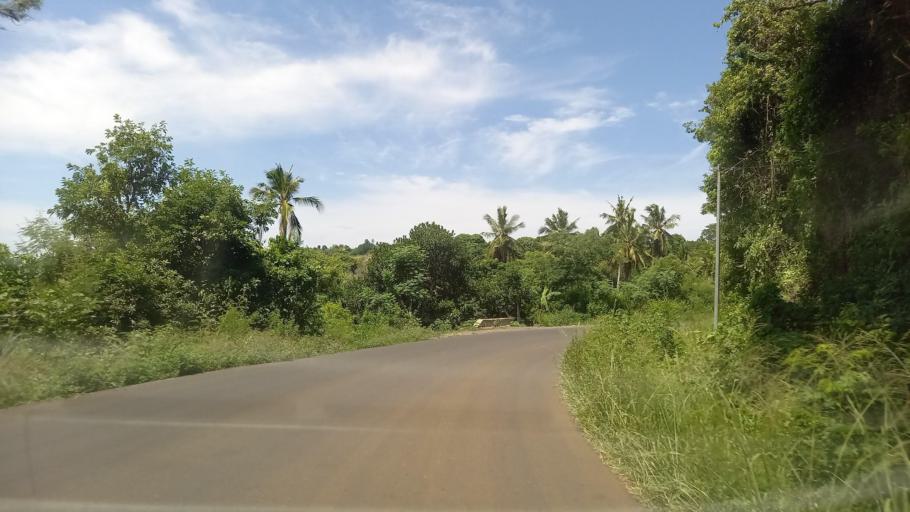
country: YT
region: M'Tsangamouji
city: M'Tsangamouji
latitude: -12.7494
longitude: 45.0609
